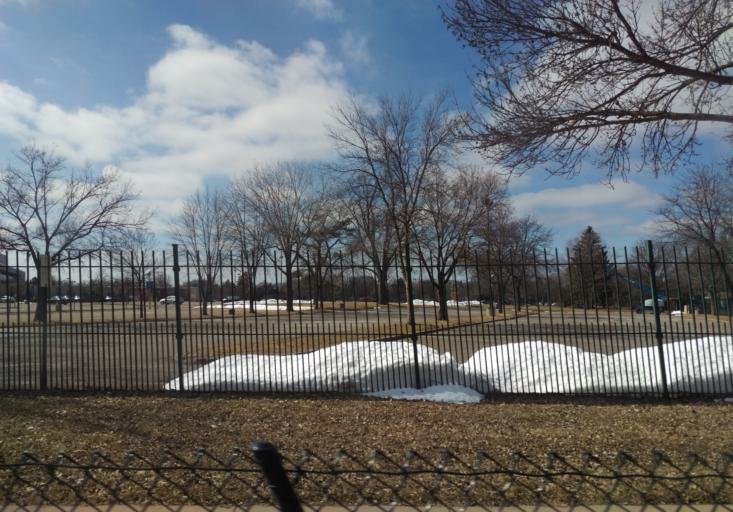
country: US
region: Minnesota
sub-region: Dakota County
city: Mendota Heights
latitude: 44.9052
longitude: -93.2033
